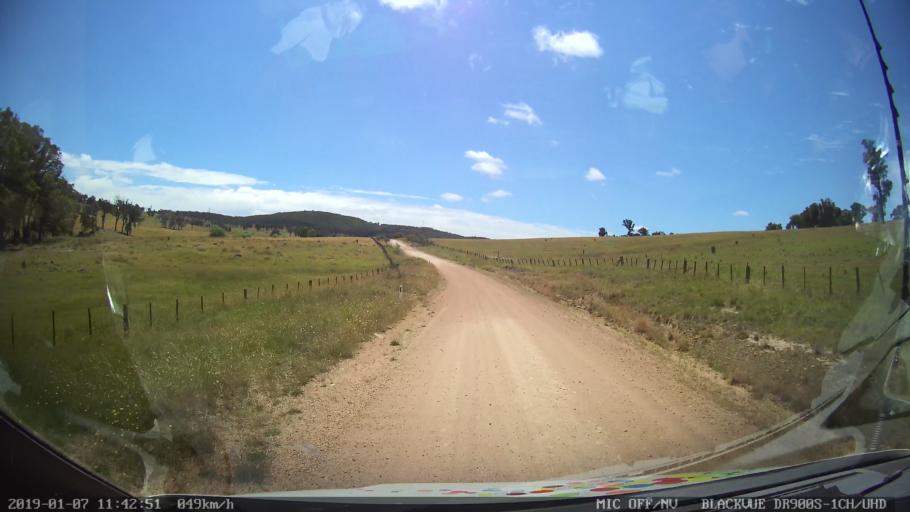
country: AU
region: New South Wales
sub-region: Guyra
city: Guyra
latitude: -30.3578
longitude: 151.5971
